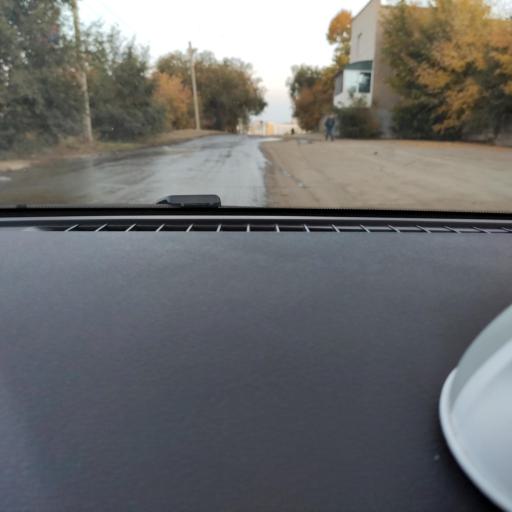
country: RU
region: Samara
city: Samara
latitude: 53.1822
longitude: 50.1436
